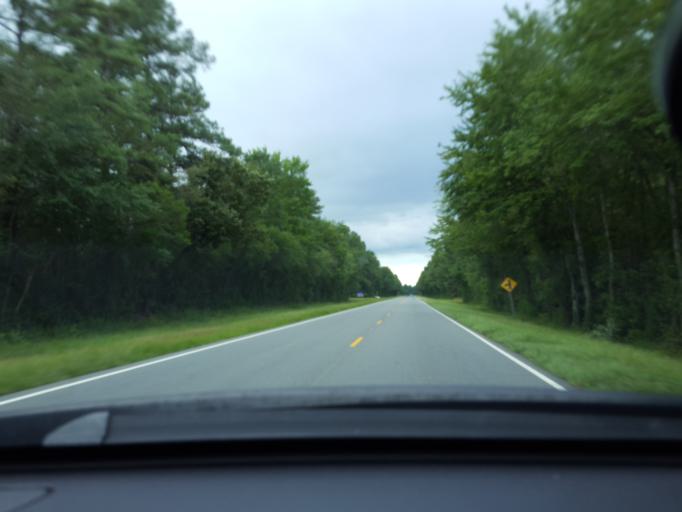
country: US
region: North Carolina
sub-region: Bladen County
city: Elizabethtown
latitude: 34.7266
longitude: -78.4398
